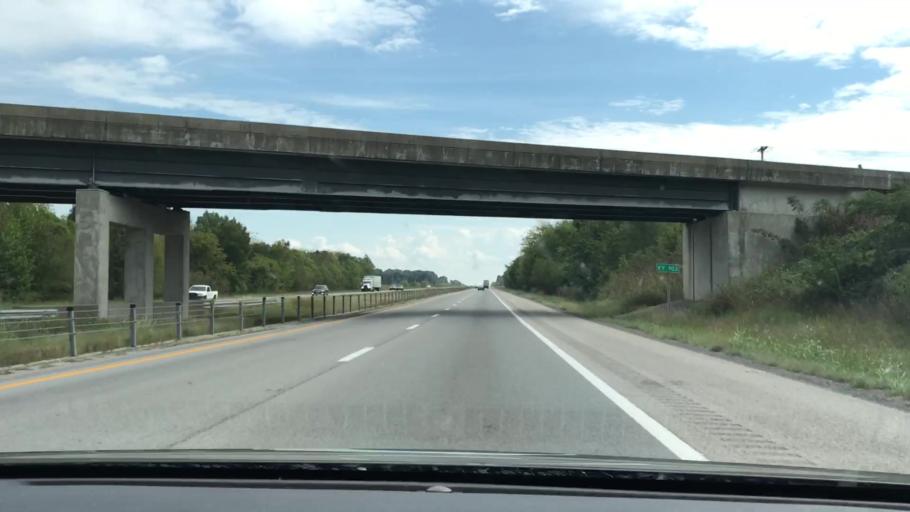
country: US
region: Kentucky
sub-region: Caldwell County
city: Princeton
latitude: 36.9909
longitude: -87.9393
